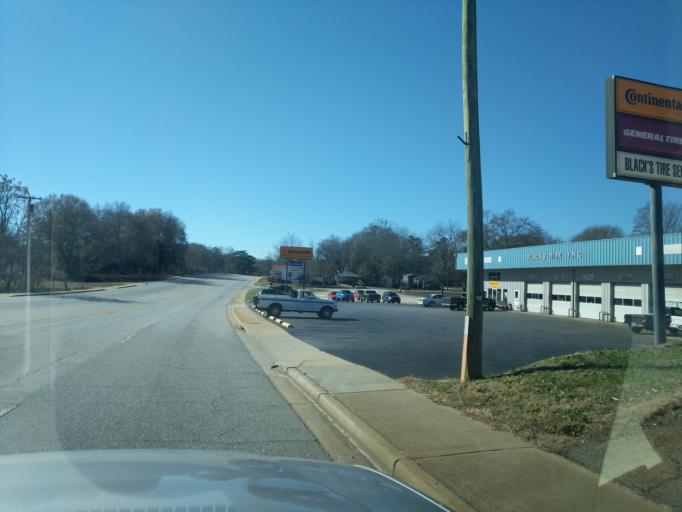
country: US
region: South Carolina
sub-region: Oconee County
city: Westminster
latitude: 34.6598
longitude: -83.0814
